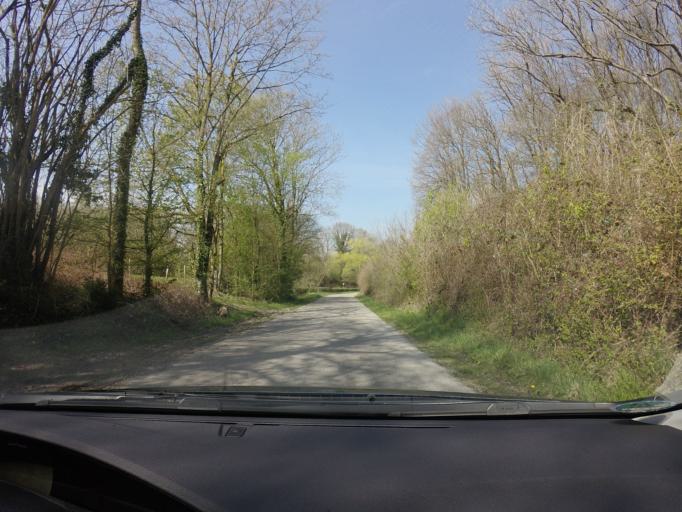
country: NL
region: Limburg
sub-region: Valkenburg aan de Geul
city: Berg
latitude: 50.8398
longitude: 5.7721
